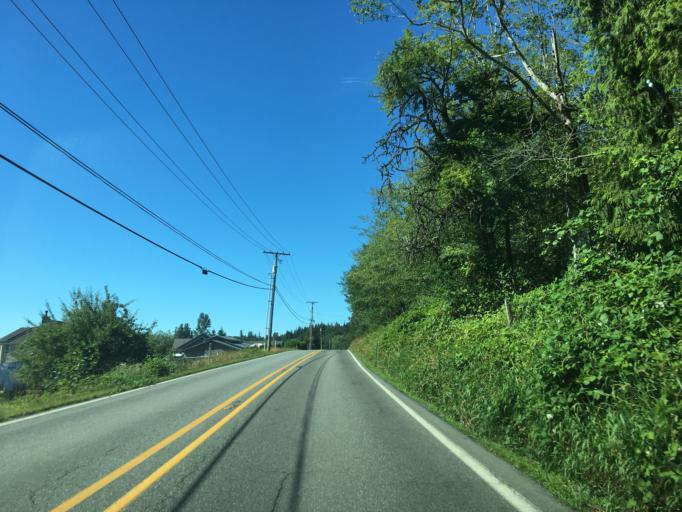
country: US
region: Washington
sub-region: Skagit County
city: Big Lake
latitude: 48.3696
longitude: -122.2124
